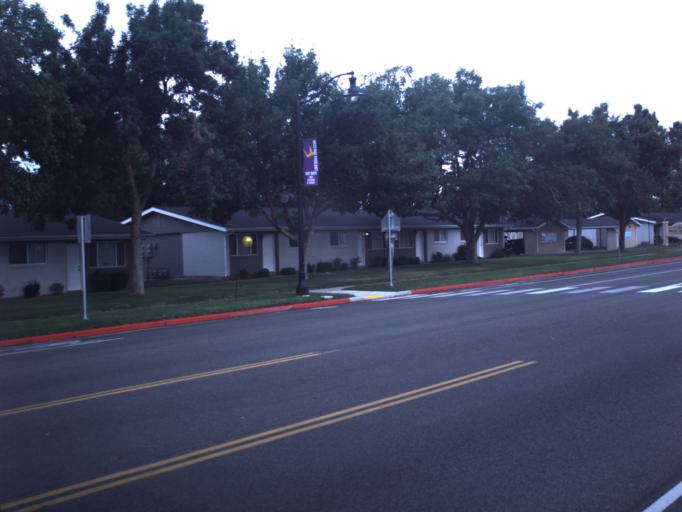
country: US
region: Utah
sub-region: Weber County
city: Roy
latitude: 41.1733
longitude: -112.0261
